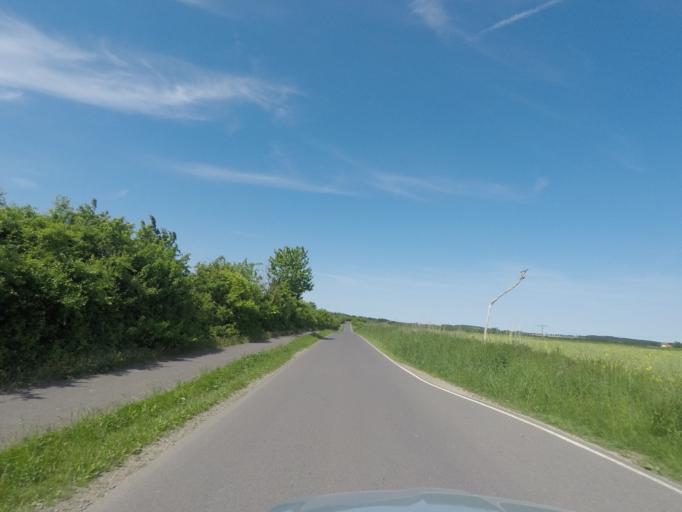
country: DE
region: Brandenburg
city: Britz
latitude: 52.8803
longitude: 13.7661
